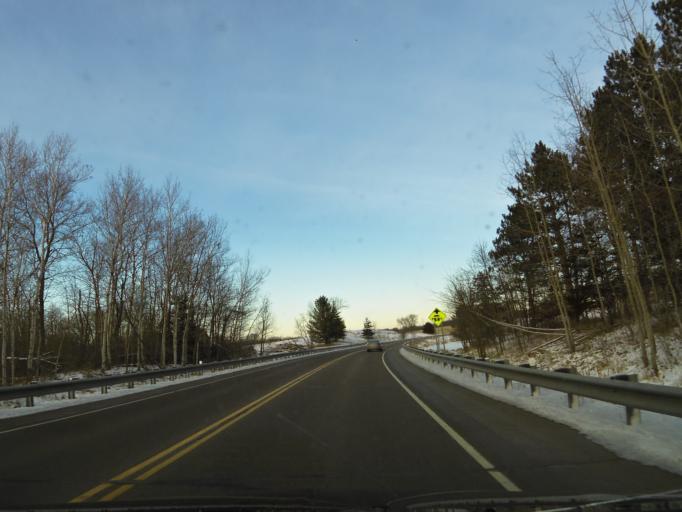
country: US
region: Wisconsin
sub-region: Polk County
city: Osceola
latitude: 45.3424
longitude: -92.7240
